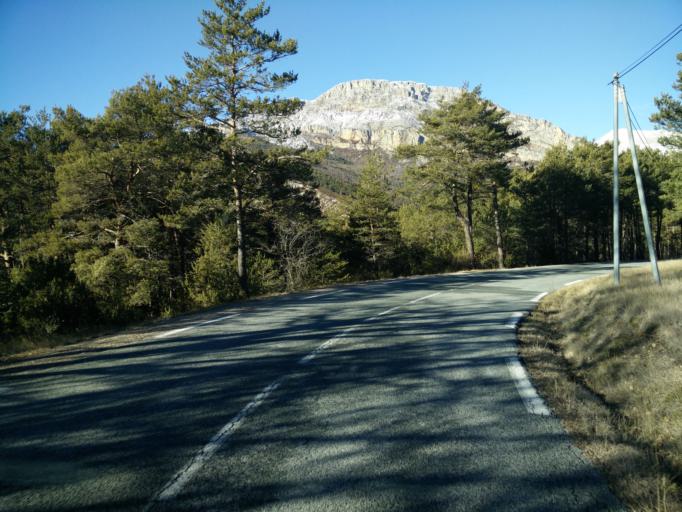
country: FR
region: Provence-Alpes-Cote d'Azur
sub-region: Departement des Alpes-de-Haute-Provence
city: Castellane
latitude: 43.7910
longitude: 6.4429
